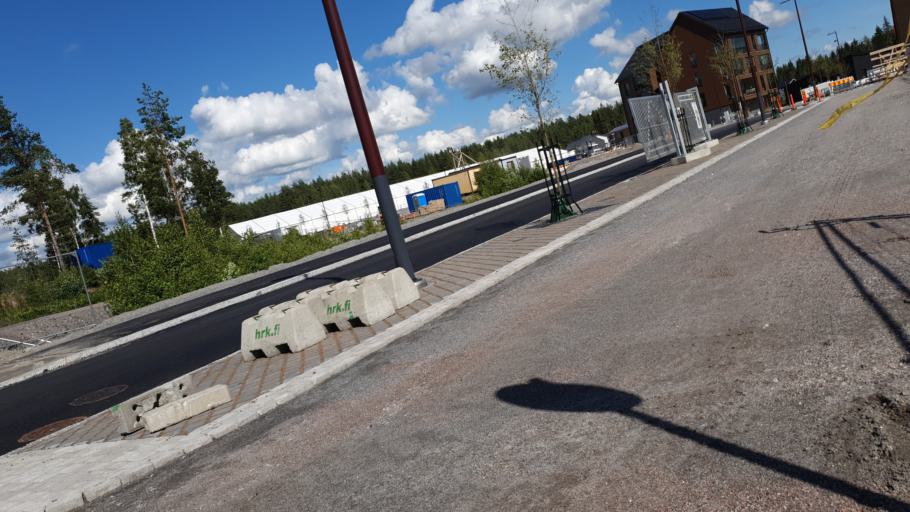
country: FI
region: Uusimaa
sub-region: Helsinki
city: Tuusula
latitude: 60.3967
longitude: 25.0463
